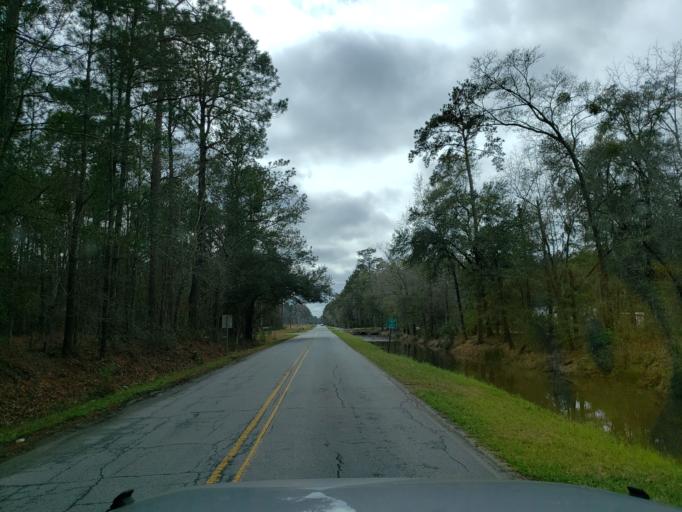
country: US
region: Georgia
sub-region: Chatham County
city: Pooler
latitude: 32.0464
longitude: -81.2900
